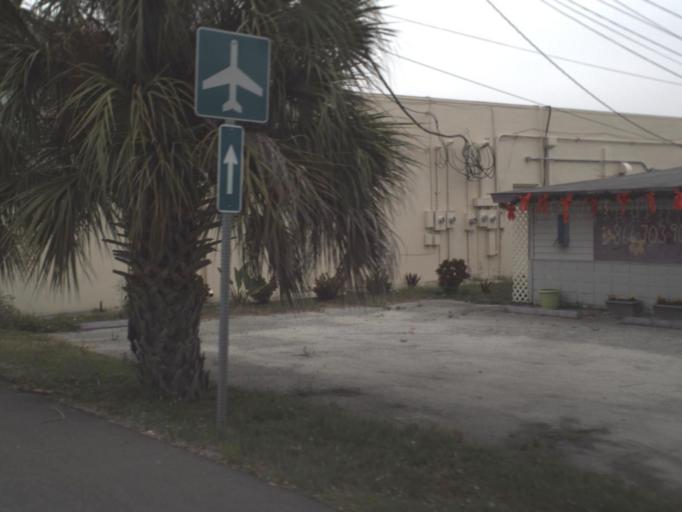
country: US
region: Florida
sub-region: Brevard County
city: Melbourne
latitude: 28.0845
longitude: -80.6270
